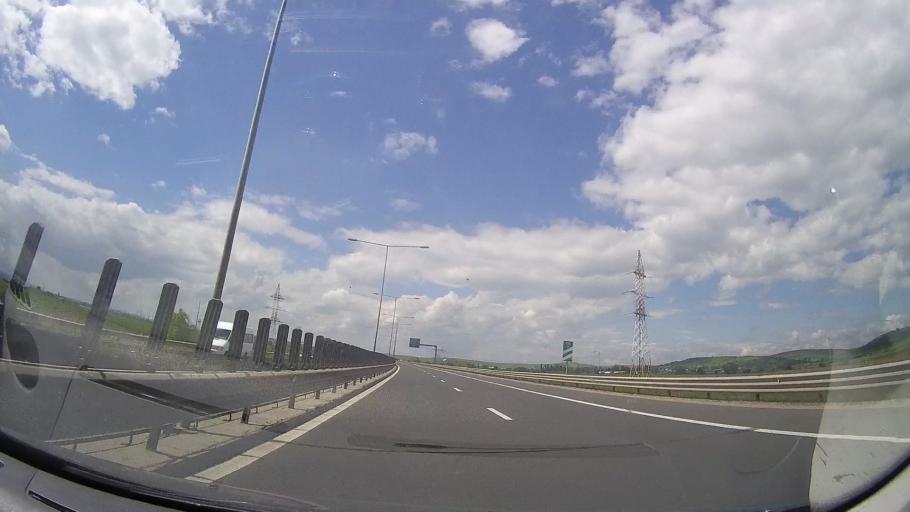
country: RO
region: Sibiu
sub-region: Municipiul Sibiu
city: Sibiu
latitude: 45.8179
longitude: 24.1635
